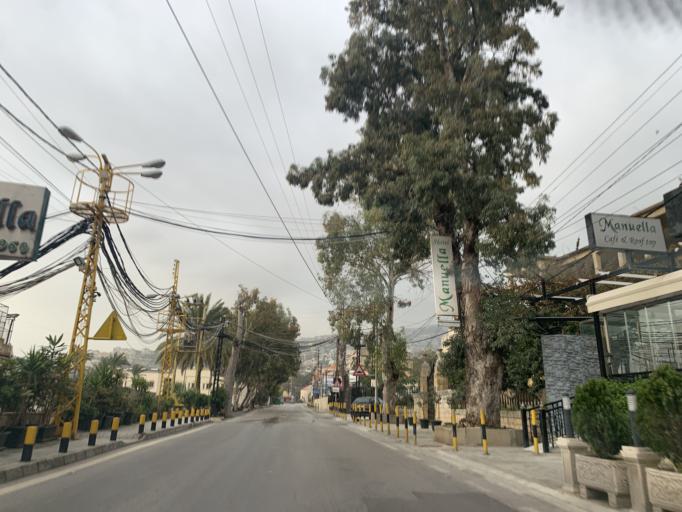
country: LB
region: Mont-Liban
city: Djounie
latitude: 34.0040
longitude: 35.6450
